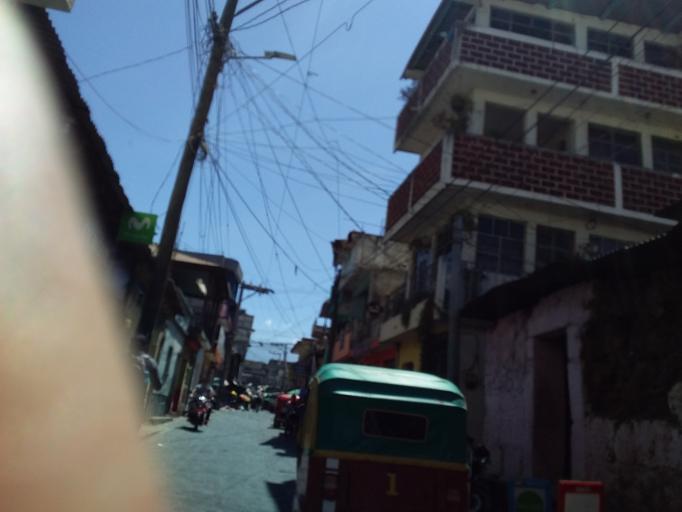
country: GT
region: Solola
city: San Pedro La Laguna
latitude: 14.6923
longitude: -91.2732
